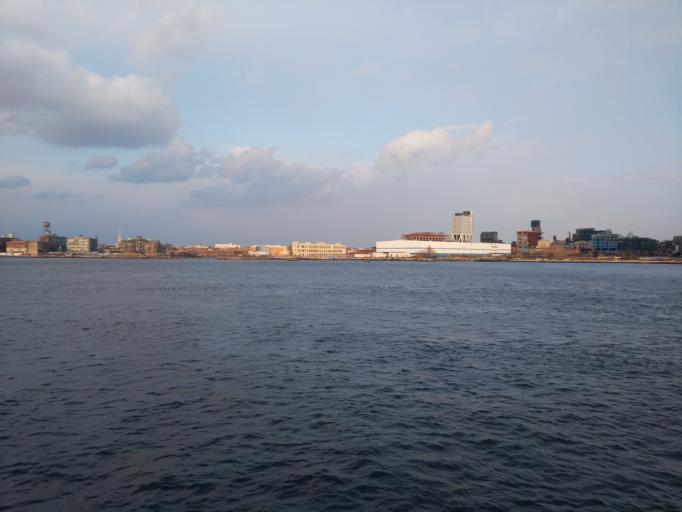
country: US
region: New York
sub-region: Queens County
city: Long Island City
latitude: 40.7237
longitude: -73.9683
